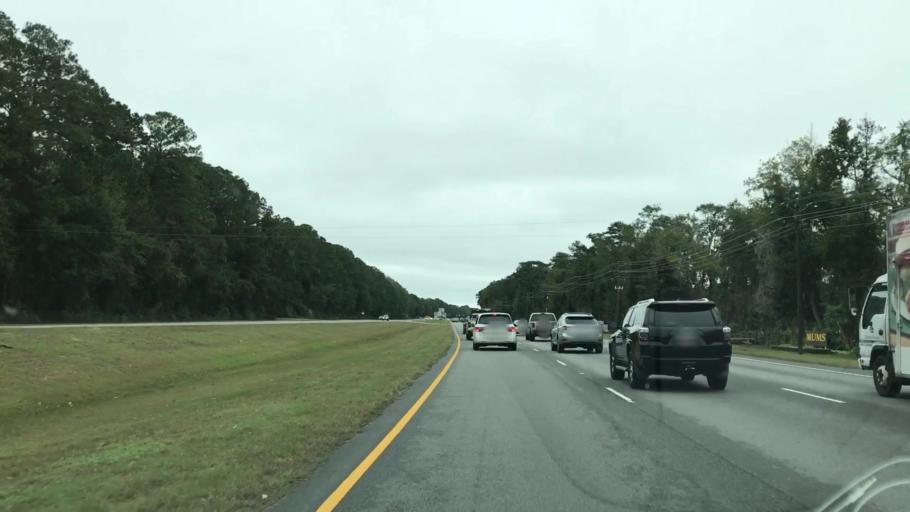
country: US
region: South Carolina
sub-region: Beaufort County
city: Bluffton
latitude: 32.2739
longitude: -80.8690
